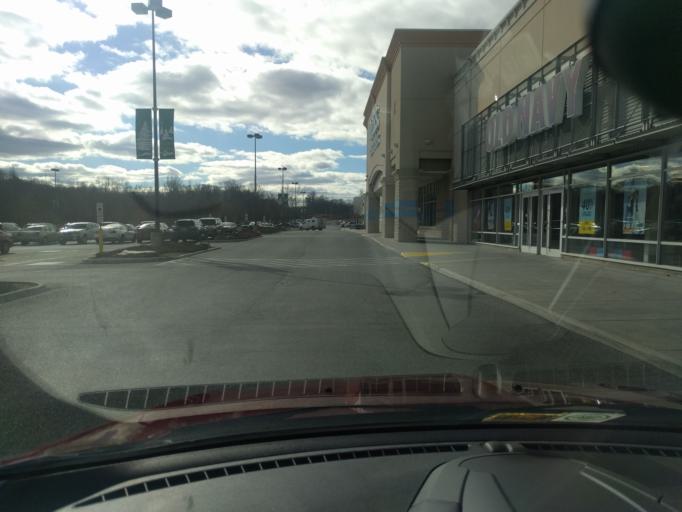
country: US
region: Virginia
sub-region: City of Lynchburg
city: West Lynchburg
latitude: 37.3431
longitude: -79.1936
